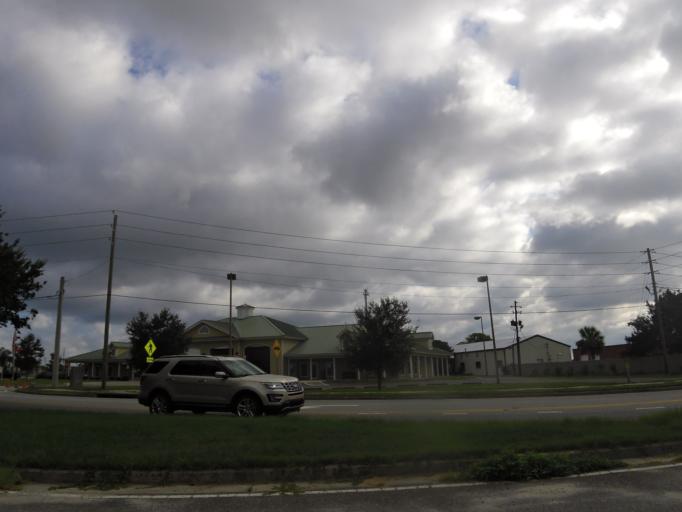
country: US
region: Georgia
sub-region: Glynn County
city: Saint Simons Island
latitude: 31.1579
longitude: -81.3864
